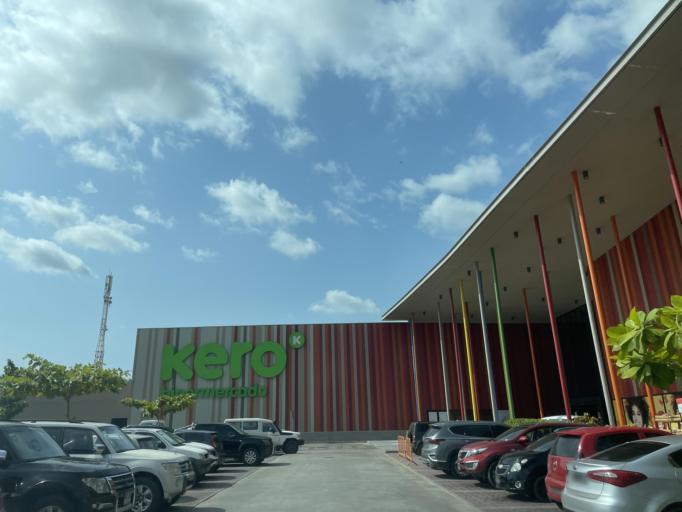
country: AO
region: Luanda
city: Luanda
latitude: -8.9909
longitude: 13.2883
